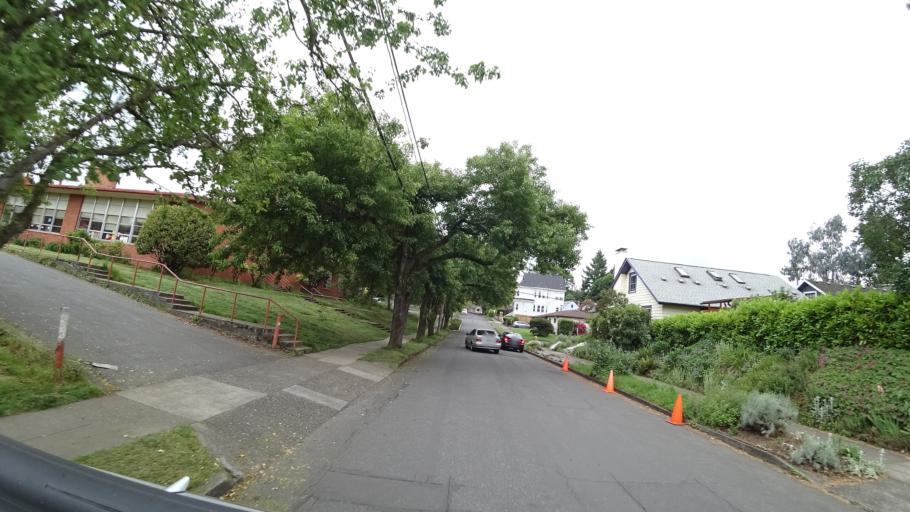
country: US
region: Oregon
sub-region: Multnomah County
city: Lents
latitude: 45.5211
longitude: -122.6049
